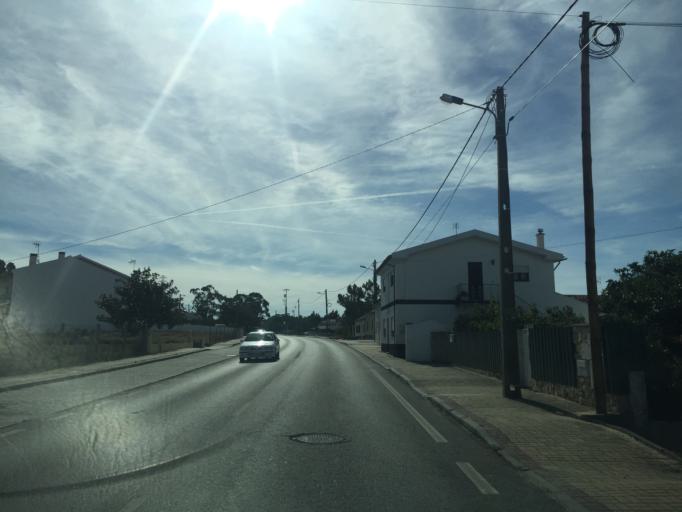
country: PT
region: Coimbra
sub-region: Figueira da Foz
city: Lavos
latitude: 40.0869
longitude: -8.8261
